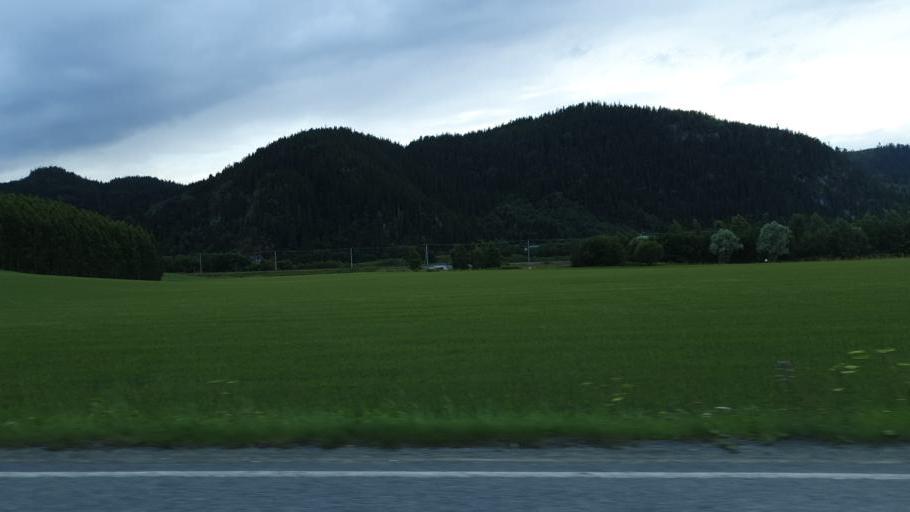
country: NO
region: Sor-Trondelag
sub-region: Melhus
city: Lundamo
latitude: 63.1959
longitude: 10.3033
